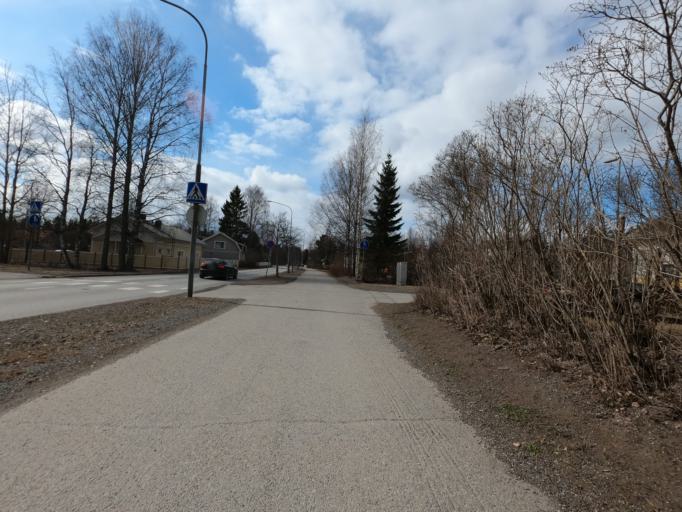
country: FI
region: North Karelia
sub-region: Joensuu
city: Joensuu
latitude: 62.6179
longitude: 29.8503
